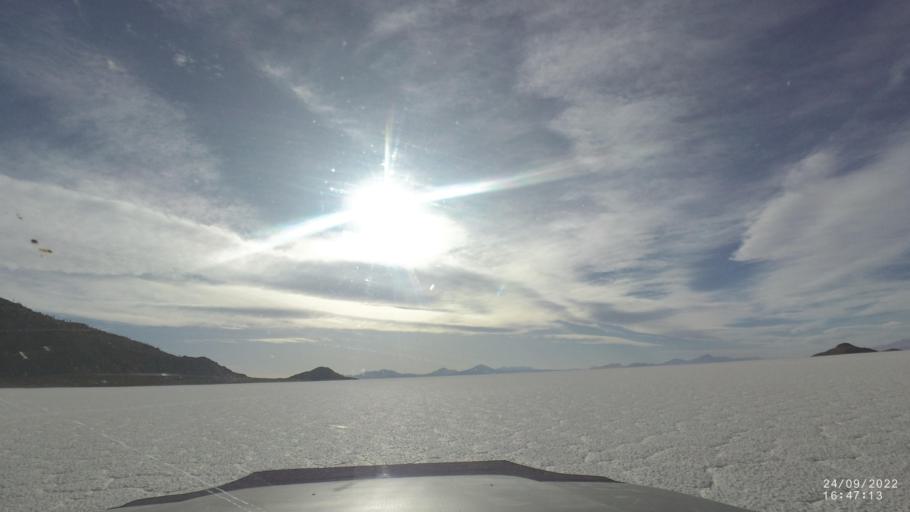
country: BO
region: Potosi
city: Colchani
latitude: -20.1327
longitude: -67.8001
